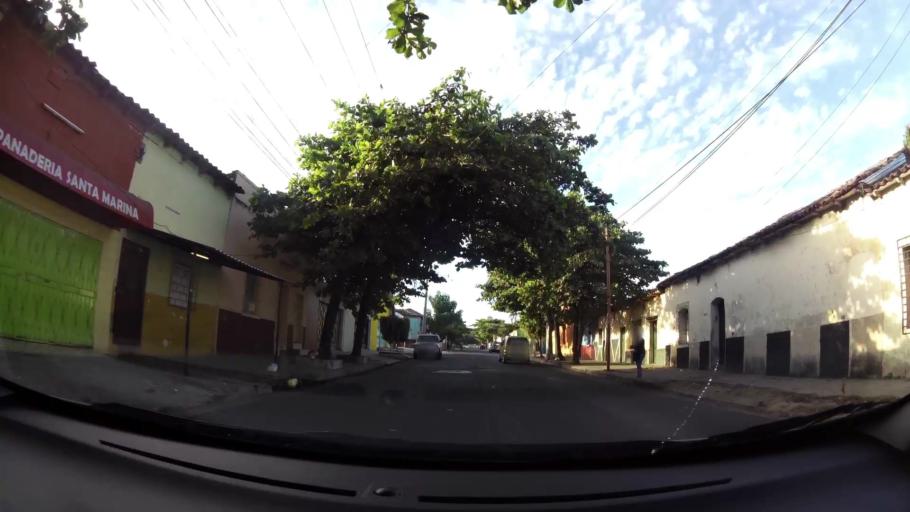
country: SV
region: Santa Ana
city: Santa Ana
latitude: 13.9922
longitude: -89.5470
